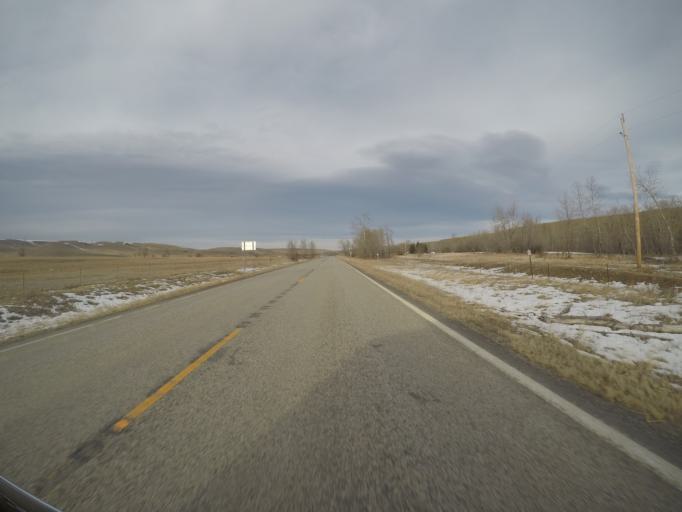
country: US
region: Montana
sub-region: Stillwater County
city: Absarokee
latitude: 45.4182
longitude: -109.4726
